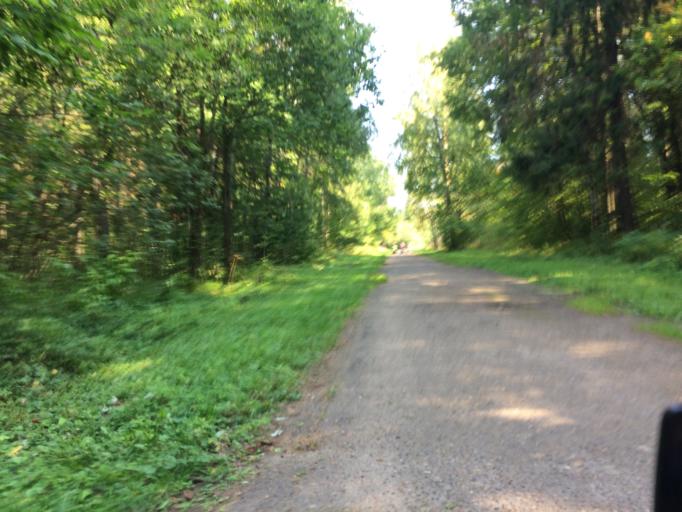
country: RU
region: Mariy-El
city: Yoshkar-Ola
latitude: 56.6173
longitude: 47.9360
